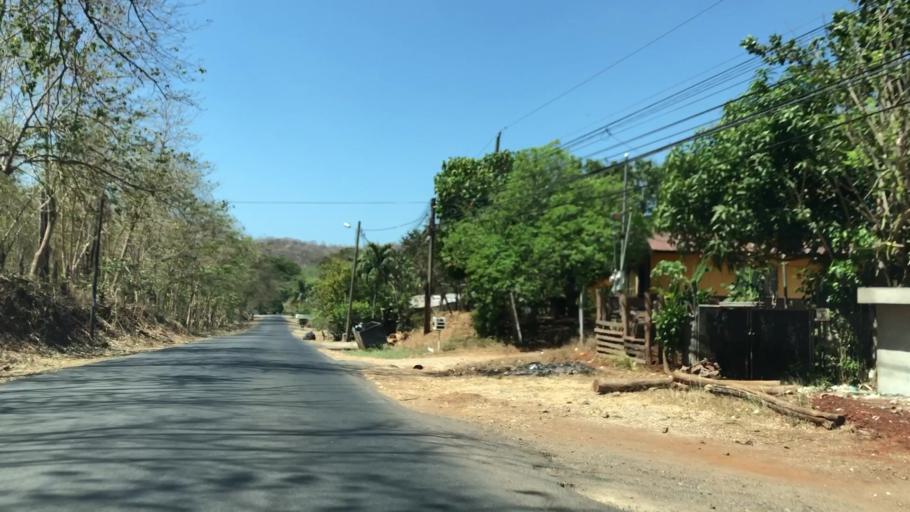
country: CR
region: Guanacaste
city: Sardinal
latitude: 10.3640
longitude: -85.8058
